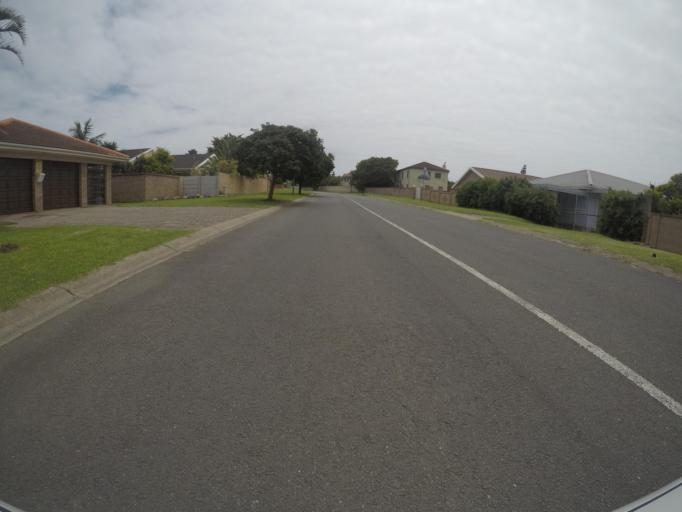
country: ZA
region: Eastern Cape
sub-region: Buffalo City Metropolitan Municipality
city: East London
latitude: -32.9777
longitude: 27.9529
